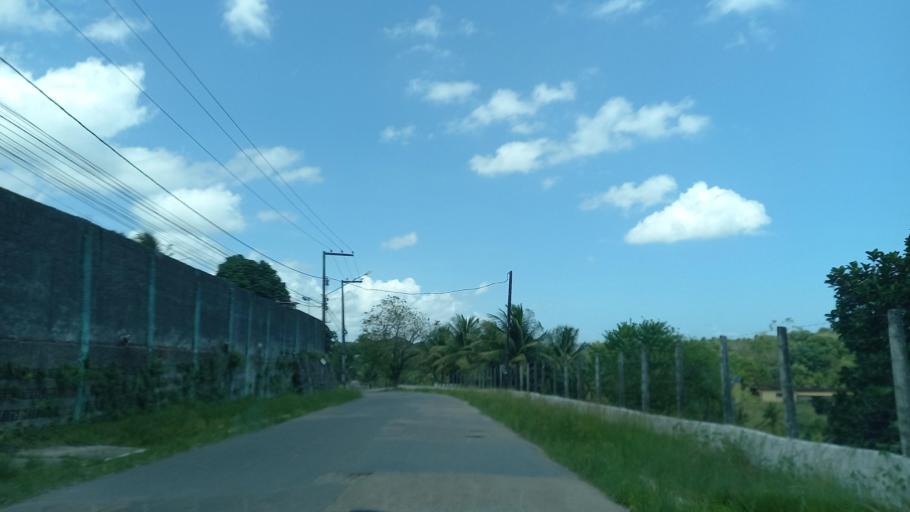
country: BR
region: Pernambuco
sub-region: Jaboatao Dos Guararapes
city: Jaboatao
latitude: -8.1685
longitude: -34.9968
